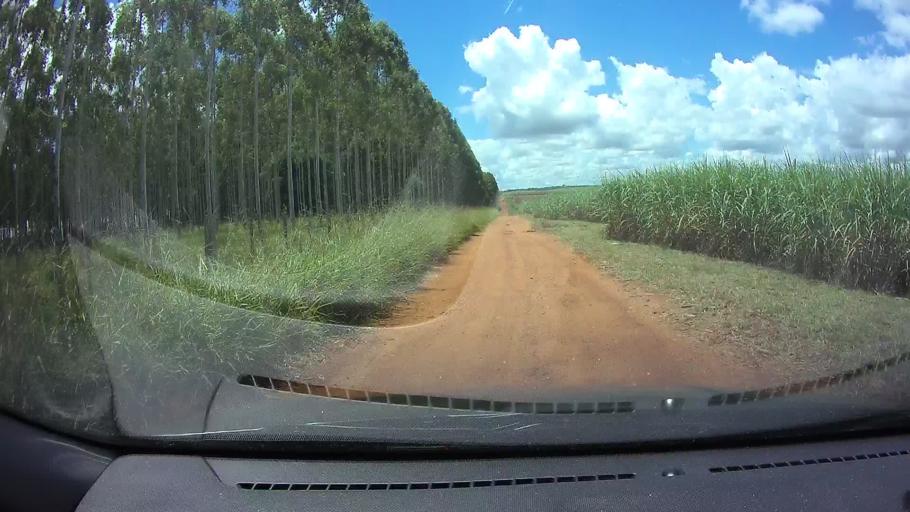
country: PY
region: Paraguari
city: La Colmena
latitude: -25.9632
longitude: -56.7321
